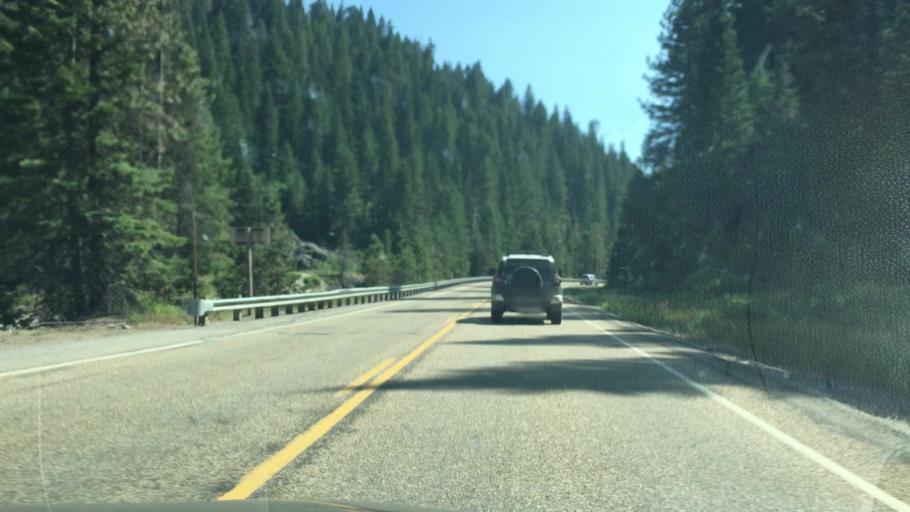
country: US
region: Idaho
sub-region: Valley County
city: Cascade
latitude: 44.2276
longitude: -116.1037
